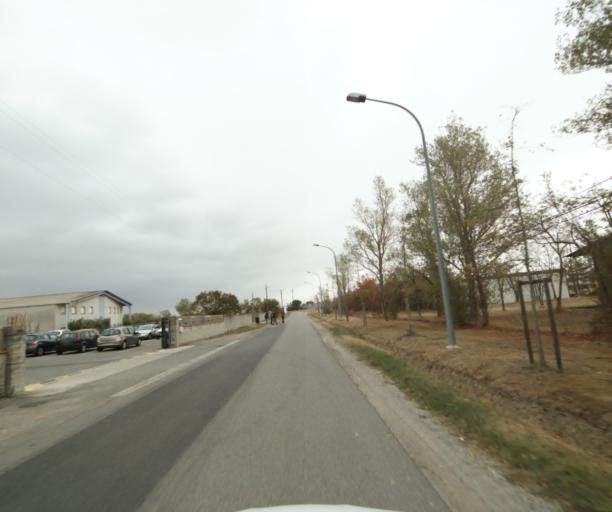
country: FR
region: Midi-Pyrenees
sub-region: Departement de la Haute-Garonne
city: Villefranche-de-Lauragais
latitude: 43.4048
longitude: 1.7011
